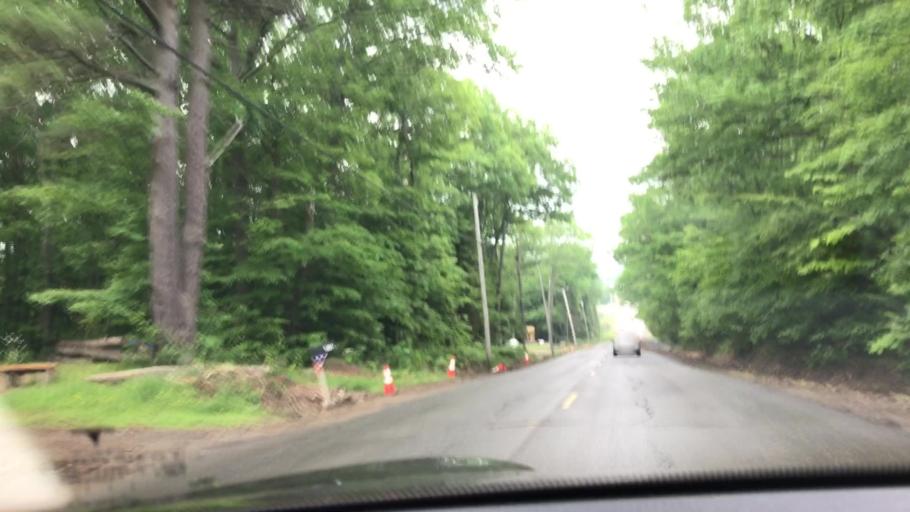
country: US
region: Maine
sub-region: Penobscot County
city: Orono
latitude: 44.8980
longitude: -68.6965
